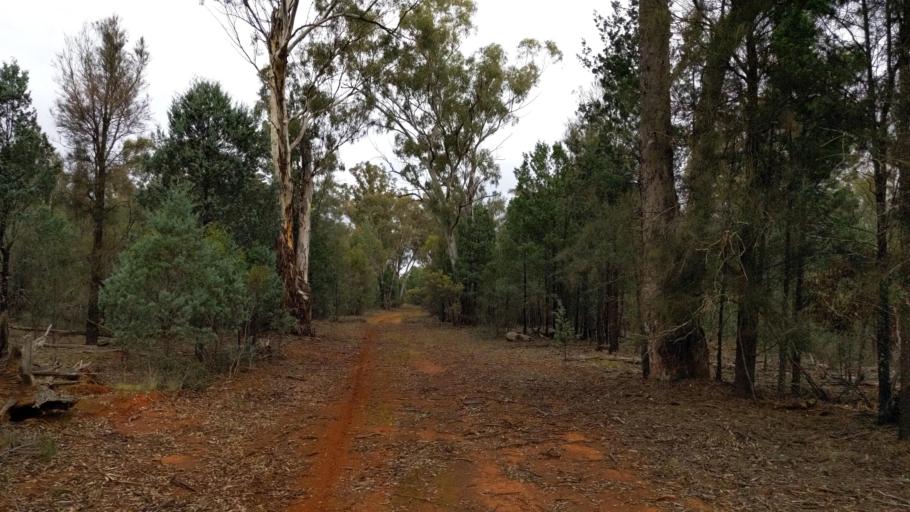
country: AU
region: New South Wales
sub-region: Coolamon
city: Coolamon
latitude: -34.8408
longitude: 146.9337
